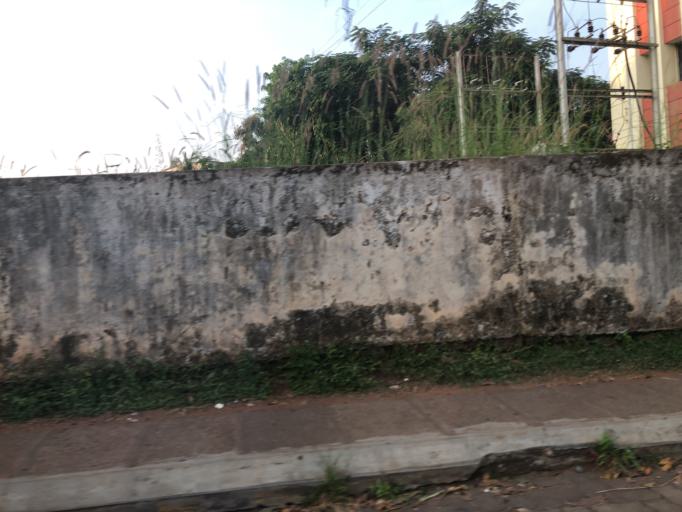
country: IN
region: Karnataka
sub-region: Dakshina Kannada
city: Mangalore
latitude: 12.8722
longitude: 74.8476
